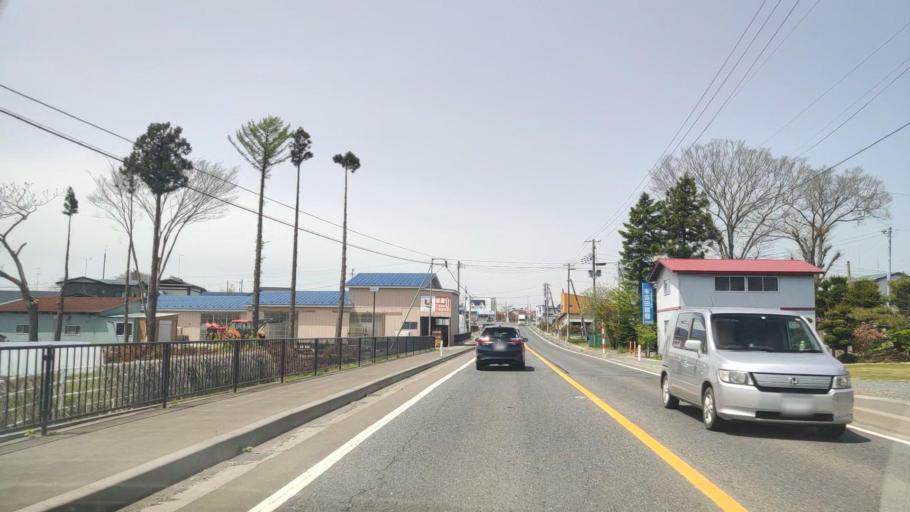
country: JP
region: Aomori
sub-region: Misawa Shi
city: Inuotose
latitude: 40.6065
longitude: 141.2894
